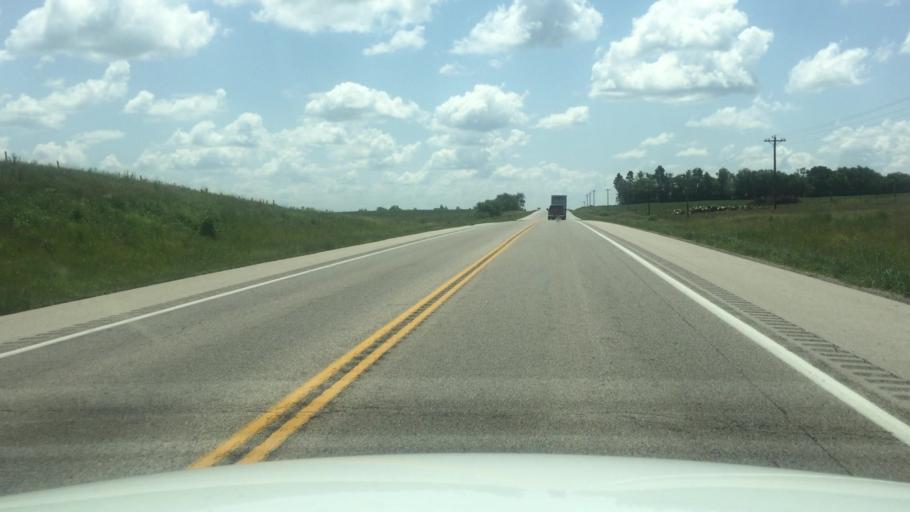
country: US
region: Kansas
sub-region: Brown County
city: Horton
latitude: 39.6777
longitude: -95.7306
